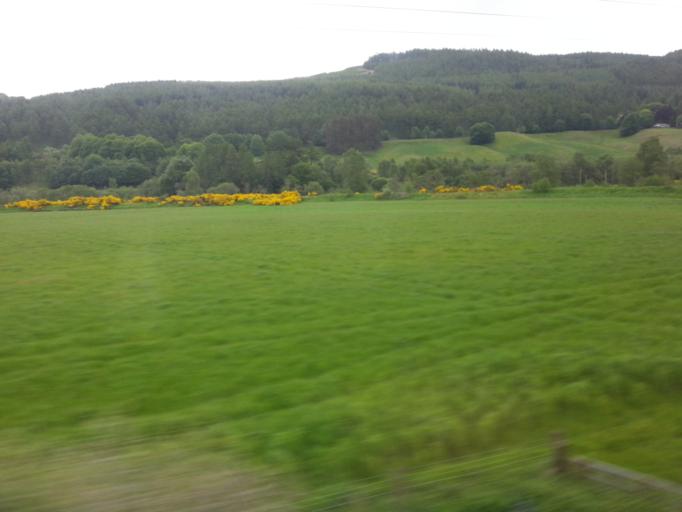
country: GB
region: Scotland
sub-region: Perth and Kinross
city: Pitlochry
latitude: 56.5886
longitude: -3.6295
